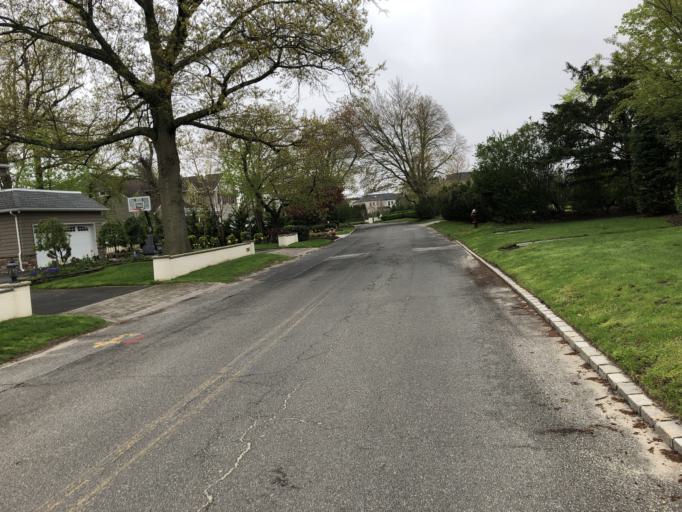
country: US
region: New York
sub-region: Nassau County
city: Hewlett Harbor
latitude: 40.6335
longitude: -73.6906
